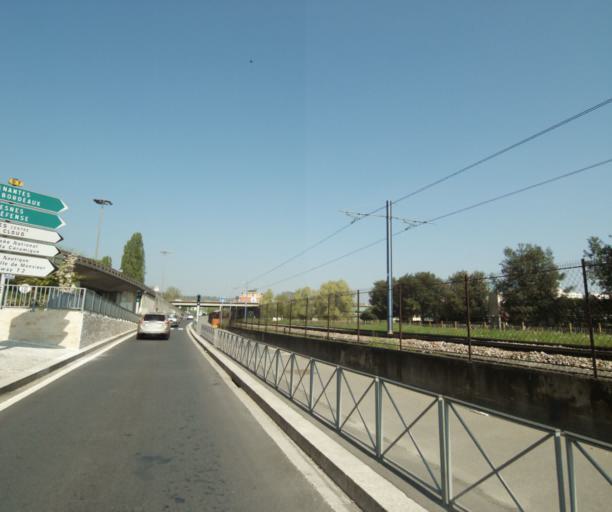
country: FR
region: Ile-de-France
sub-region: Departement des Hauts-de-Seine
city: Sevres
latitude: 48.8265
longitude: 2.2266
